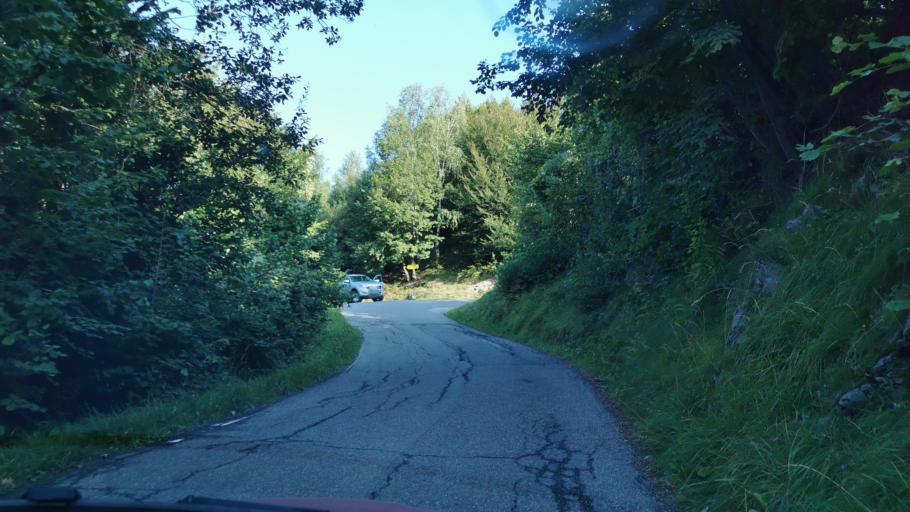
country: IT
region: Lombardy
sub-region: Provincia di Lecco
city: Moggio
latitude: 45.9137
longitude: 9.4967
